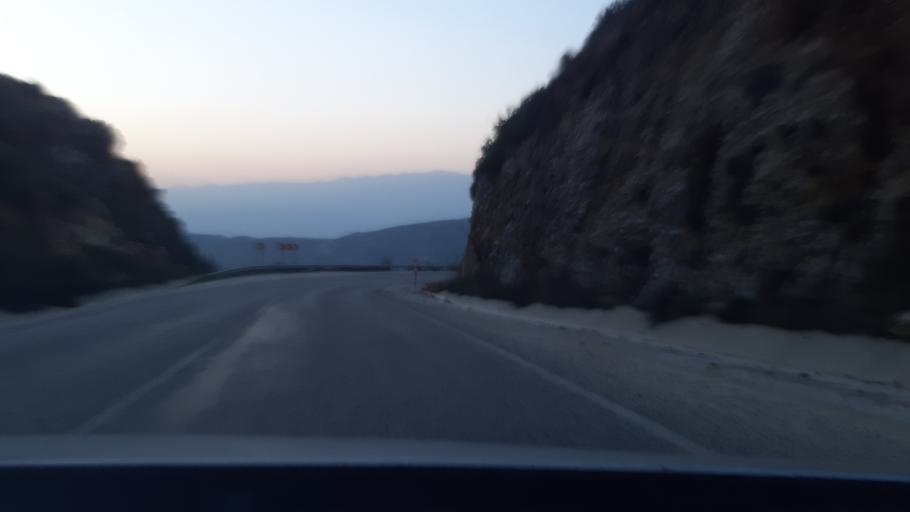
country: TR
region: Hatay
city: Dursunlu
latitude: 36.1684
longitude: 36.1870
